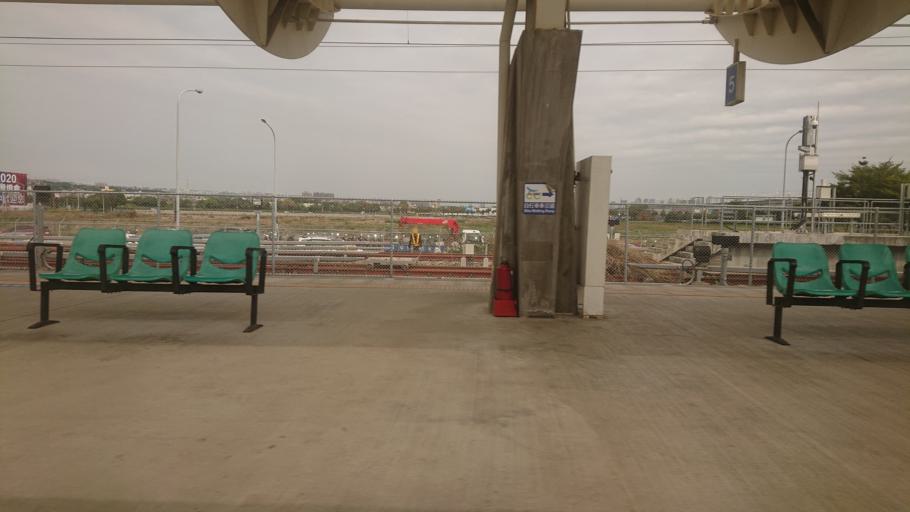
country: TW
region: Taiwan
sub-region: Changhua
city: Chang-hua
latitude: 24.1101
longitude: 120.6128
